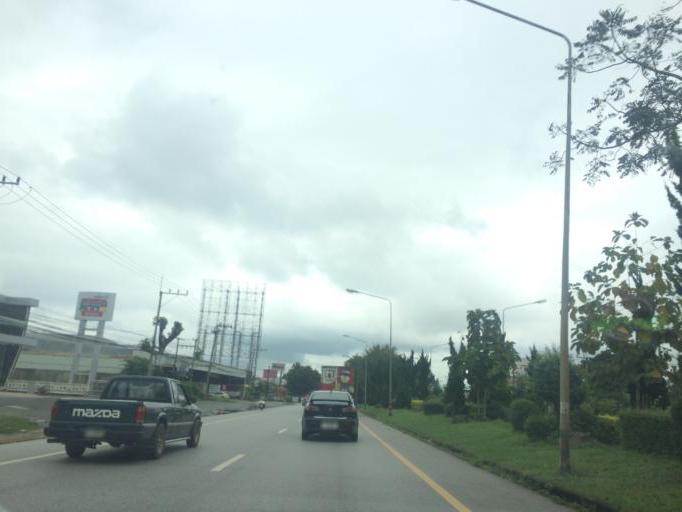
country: TH
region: Chiang Rai
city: Chiang Rai
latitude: 19.8655
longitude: 99.8229
